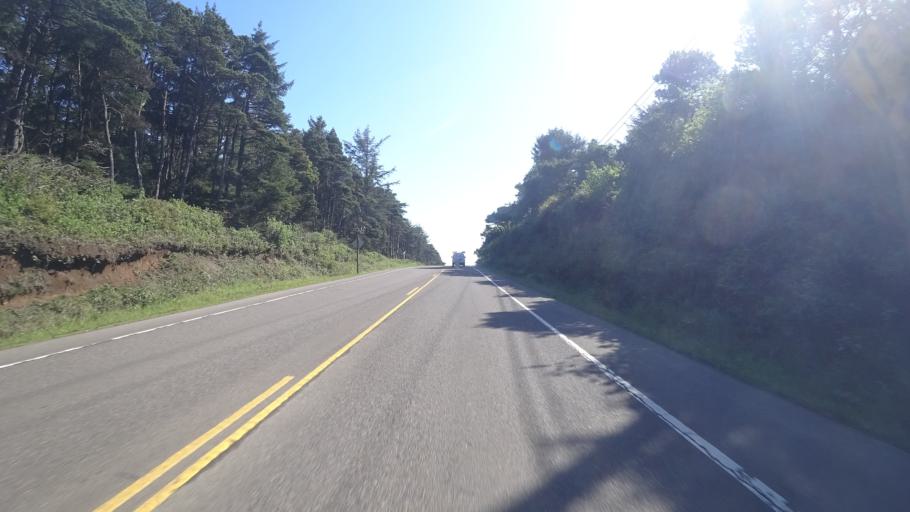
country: US
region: Oregon
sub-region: Lincoln County
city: Newport
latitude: 44.5711
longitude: -124.0677
